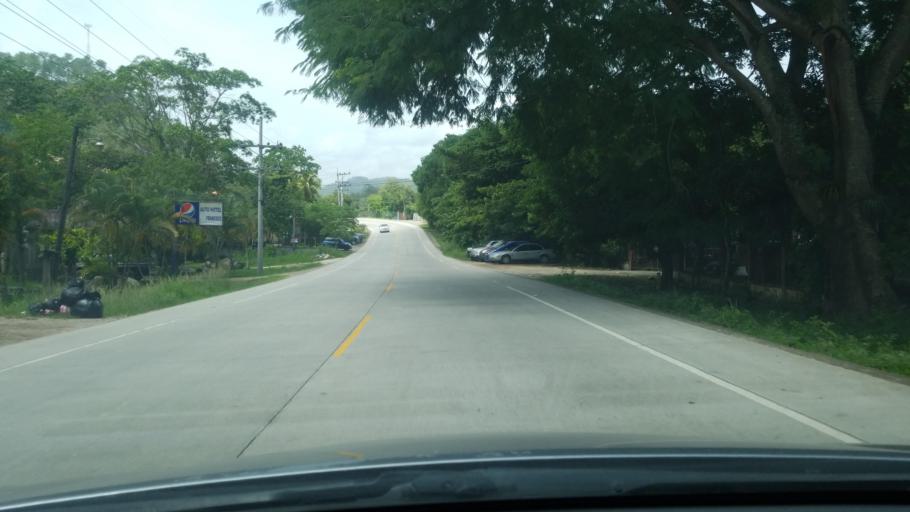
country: HN
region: Copan
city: La Entrada
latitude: 15.0435
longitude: -88.7638
